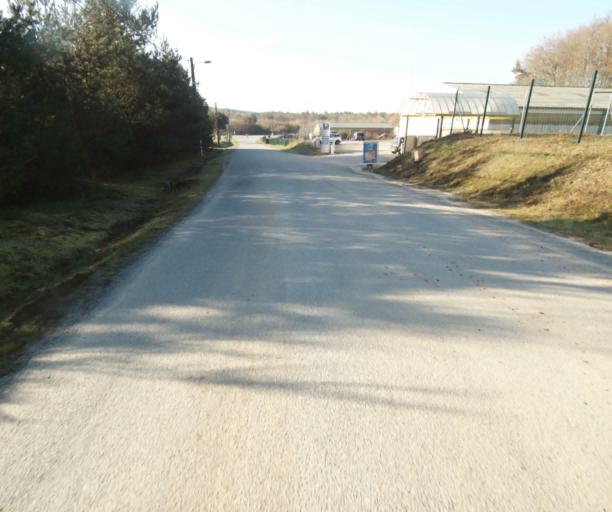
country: FR
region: Limousin
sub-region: Departement de la Correze
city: Correze
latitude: 45.3362
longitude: 1.9144
